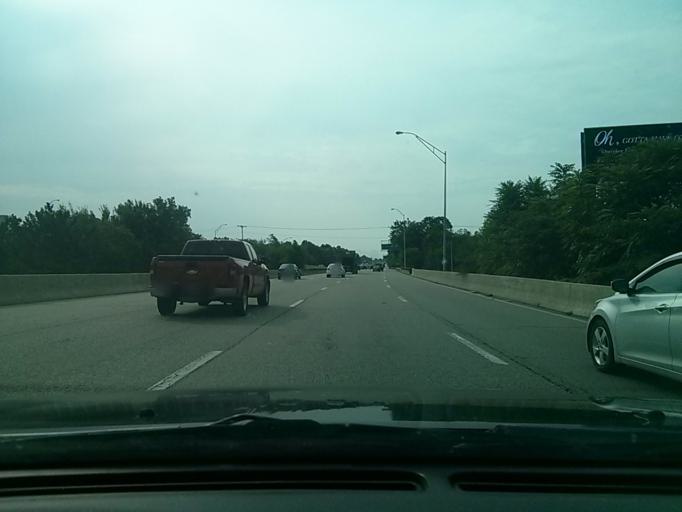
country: US
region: Oklahoma
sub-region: Tulsa County
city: Tulsa
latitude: 36.1413
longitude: -95.9553
